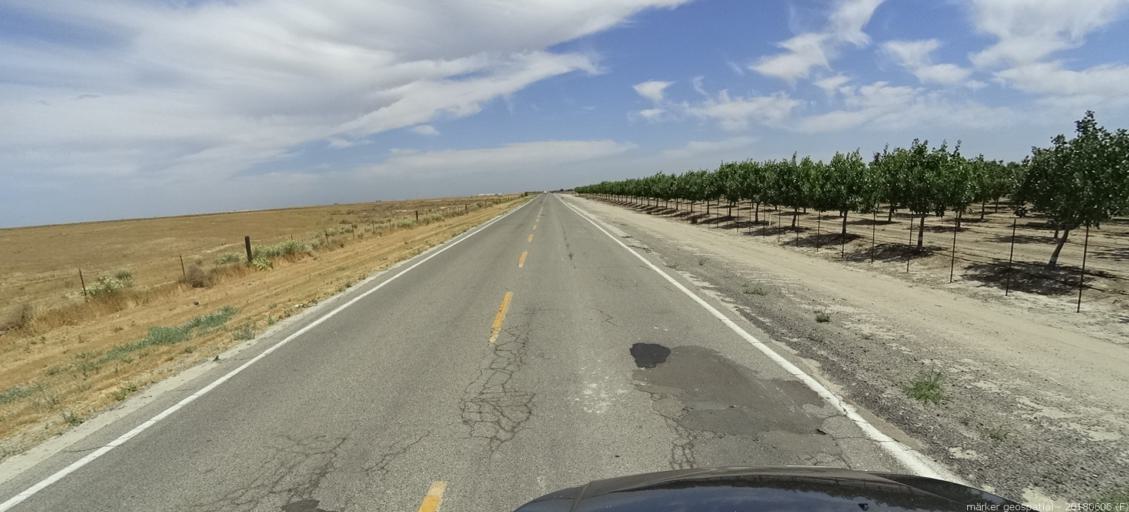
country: US
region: California
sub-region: Fresno County
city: Firebaugh
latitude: 36.8924
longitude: -120.3819
